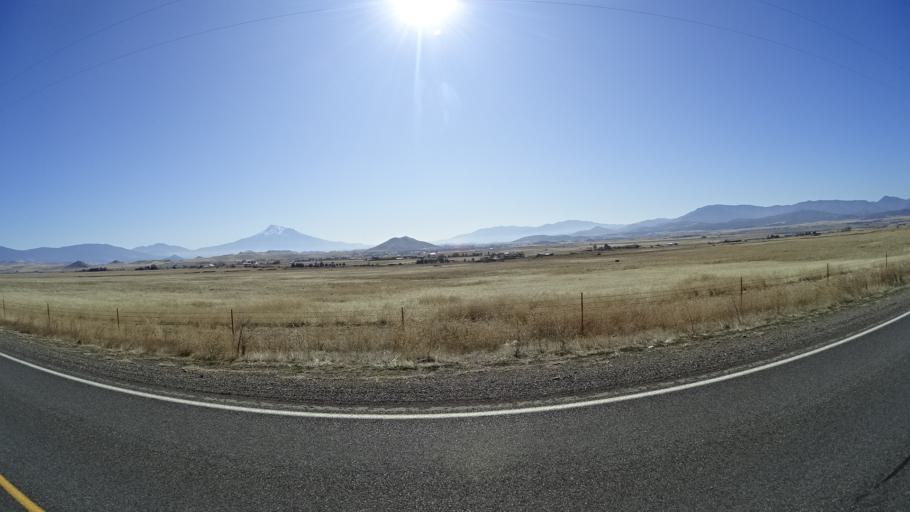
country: US
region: California
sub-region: Siskiyou County
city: Montague
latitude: 41.7709
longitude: -122.5404
